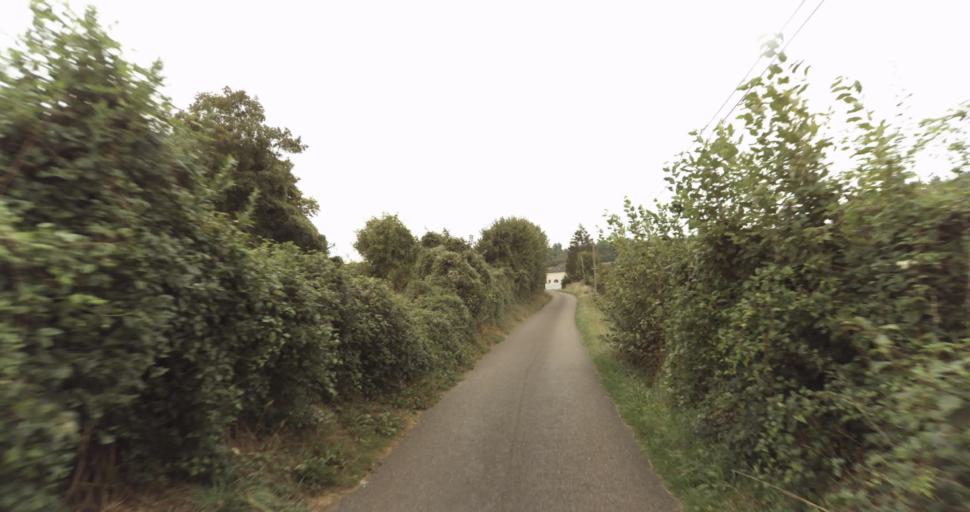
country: FR
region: Lower Normandy
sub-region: Departement de l'Orne
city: Gace
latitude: 48.8034
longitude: 0.3252
